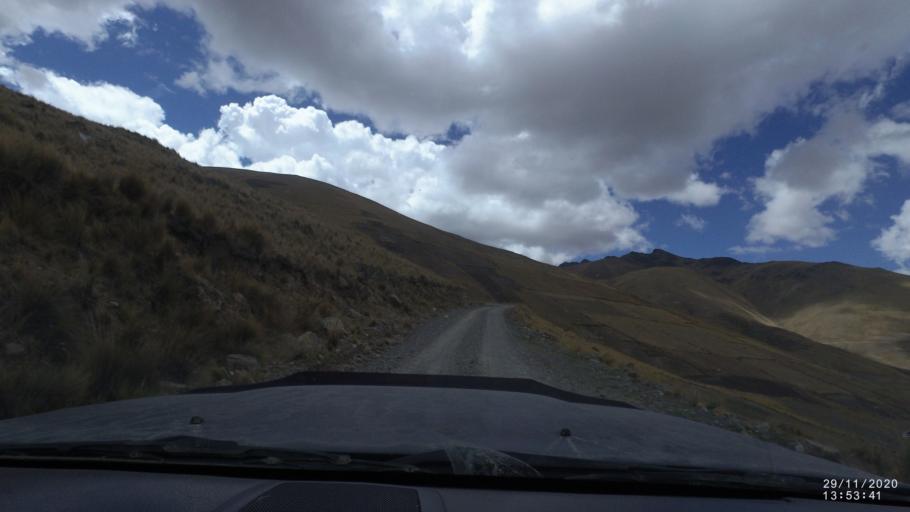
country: BO
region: Cochabamba
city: Sipe Sipe
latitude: -17.1728
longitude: -66.3538
